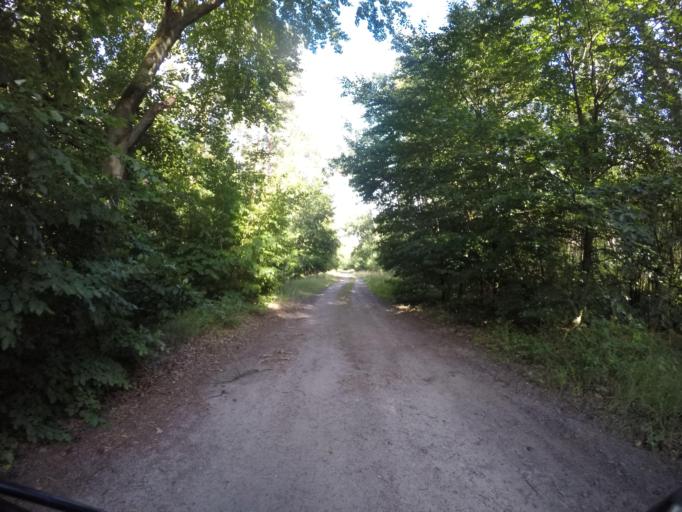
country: DE
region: Mecklenburg-Vorpommern
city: Lubtheen
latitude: 53.2635
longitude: 10.9932
